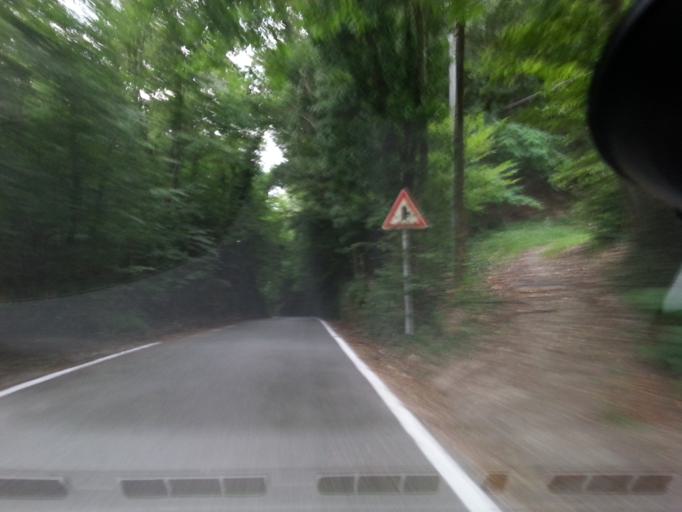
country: IT
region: Piedmont
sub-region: Provincia di Torino
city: Valgioie
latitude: 45.0763
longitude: 7.3592
